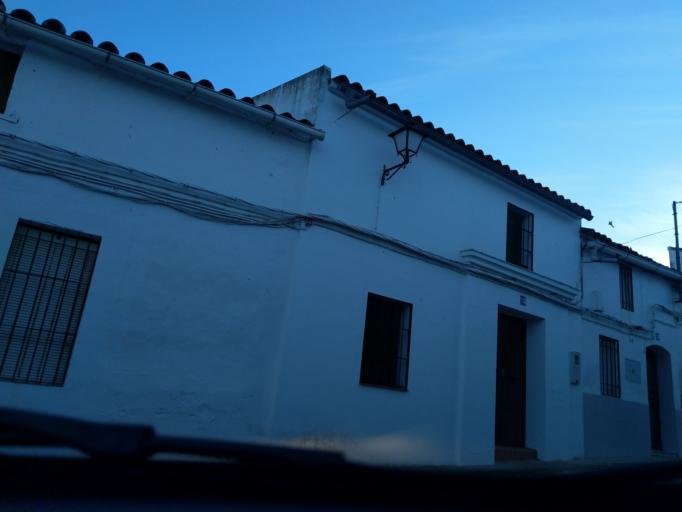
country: ES
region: Extremadura
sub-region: Provincia de Badajoz
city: Valverde de Llerena
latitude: 38.2142
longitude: -5.8233
